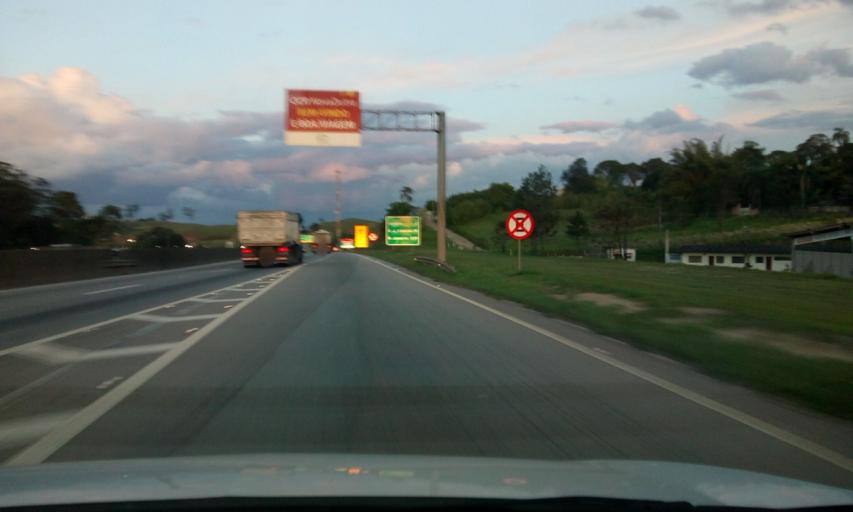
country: BR
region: Sao Paulo
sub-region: Jacarei
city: Jacarei
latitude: -23.3073
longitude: -46.0417
